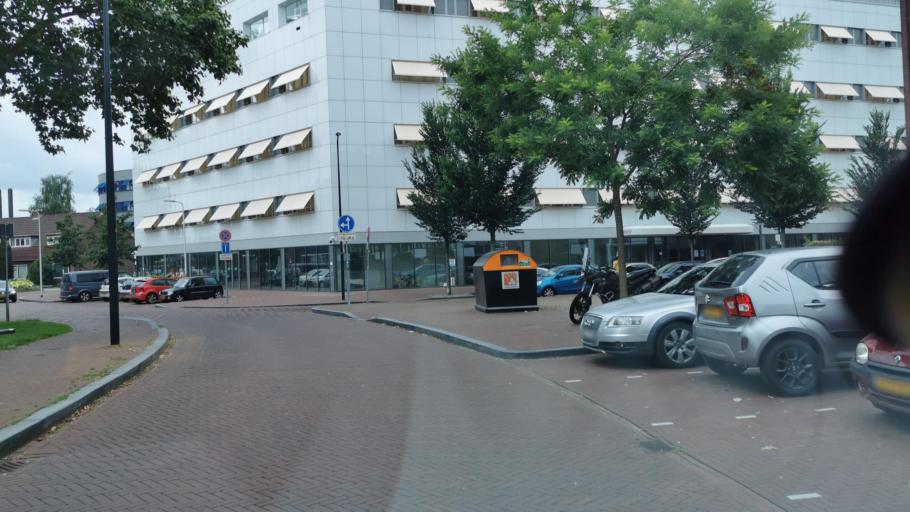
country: NL
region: Overijssel
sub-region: Gemeente Enschede
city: Enschede
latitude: 52.2163
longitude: 6.8947
